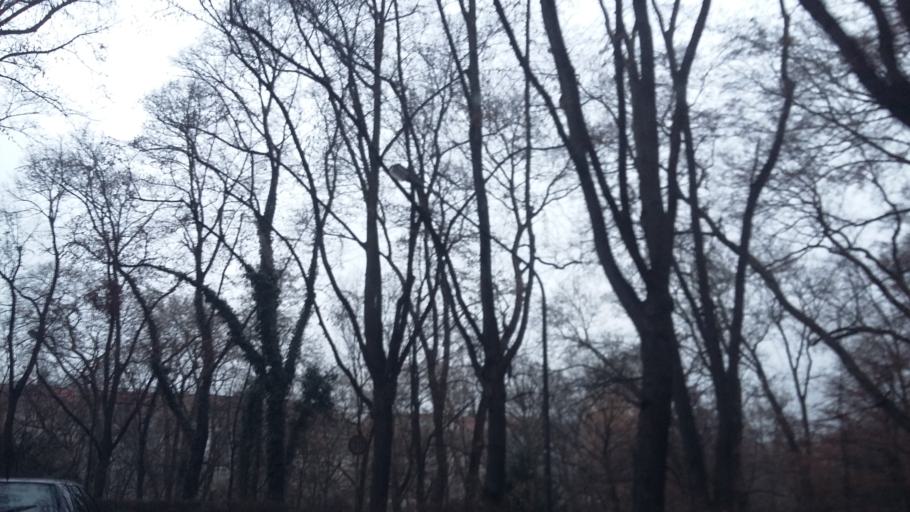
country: DE
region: Bavaria
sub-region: Upper Bavaria
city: Bogenhausen
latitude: 48.1424
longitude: 11.5970
